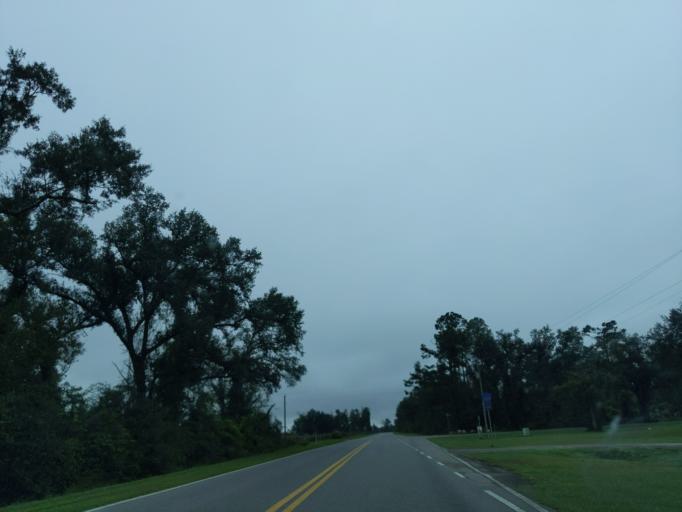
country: US
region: Florida
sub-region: Jackson County
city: Sneads
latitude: 30.6654
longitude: -84.9354
